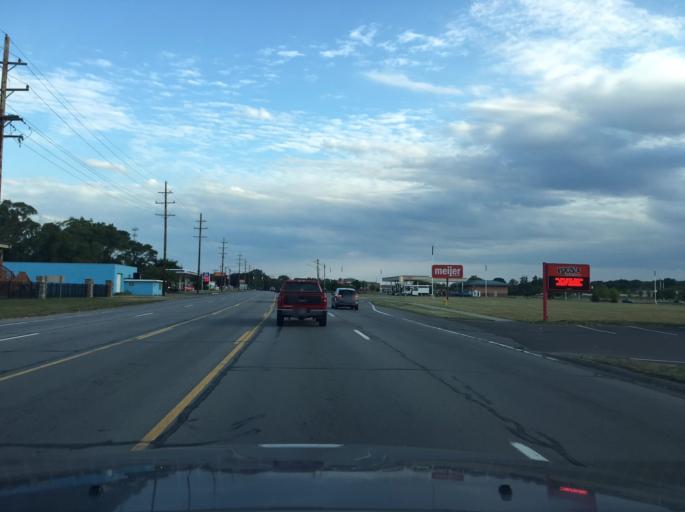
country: US
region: Michigan
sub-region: Macomb County
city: Mount Clemens
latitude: 42.5978
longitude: -82.9002
